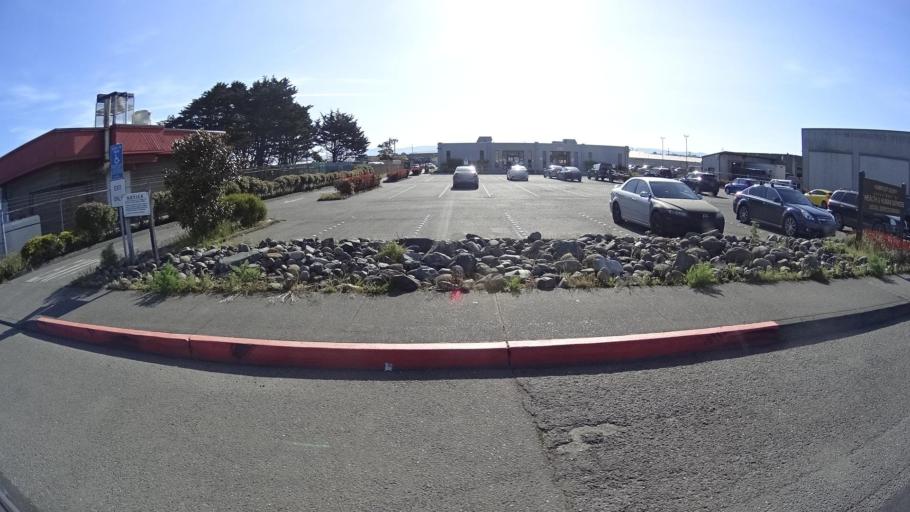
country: US
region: California
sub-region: Humboldt County
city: Eureka
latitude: 40.7978
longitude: -124.1791
